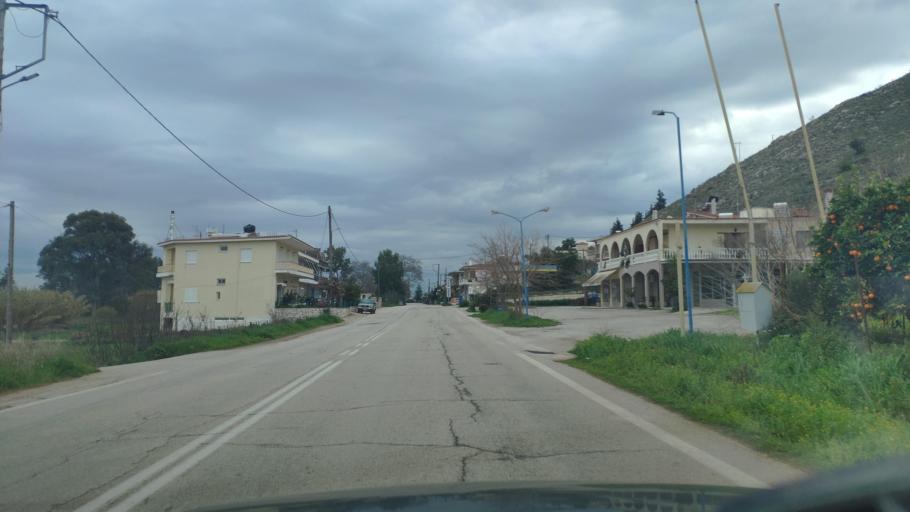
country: GR
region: Peloponnese
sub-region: Nomos Argolidos
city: Nea Kios
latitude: 37.5594
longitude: 22.7111
